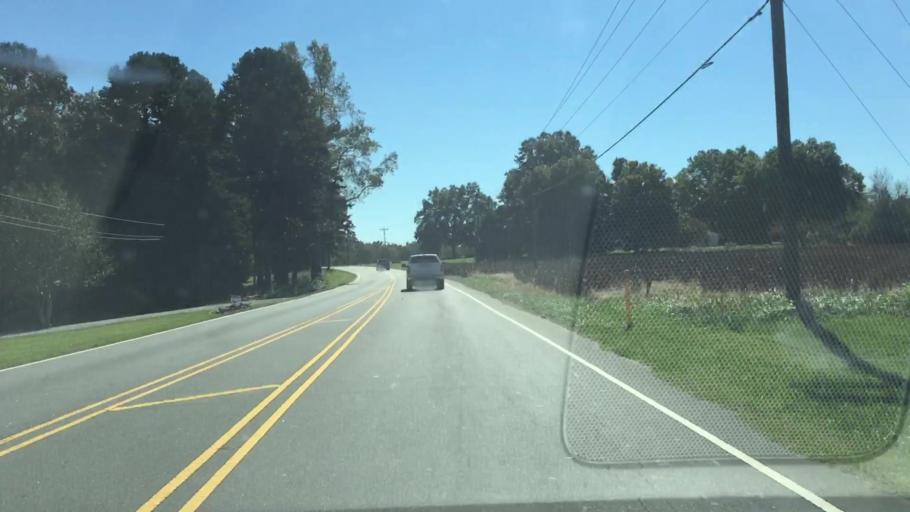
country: US
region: North Carolina
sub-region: Rowan County
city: Enochville
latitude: 35.4459
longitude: -80.7302
